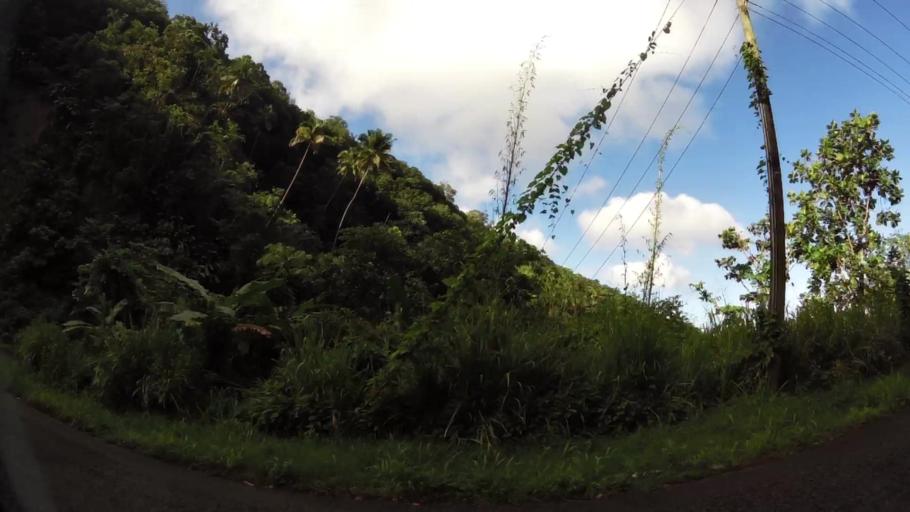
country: LC
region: Anse-la-Raye
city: Canaries
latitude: 13.9136
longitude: -61.0467
